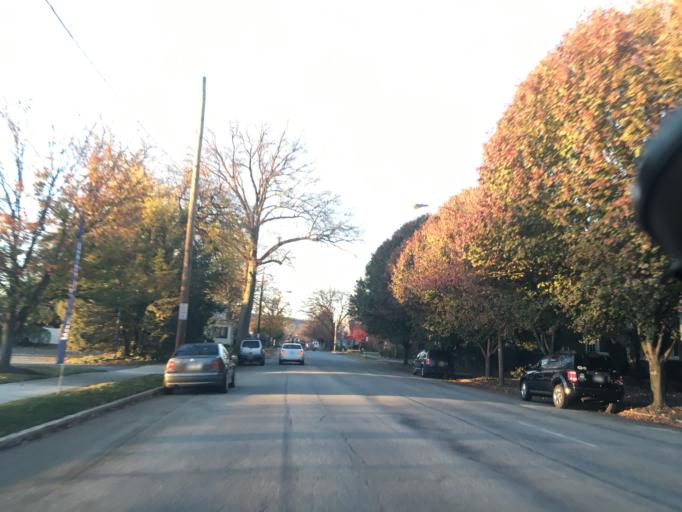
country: US
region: Pennsylvania
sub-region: Cumberland County
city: West Fairview
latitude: 40.2869
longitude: -76.9026
